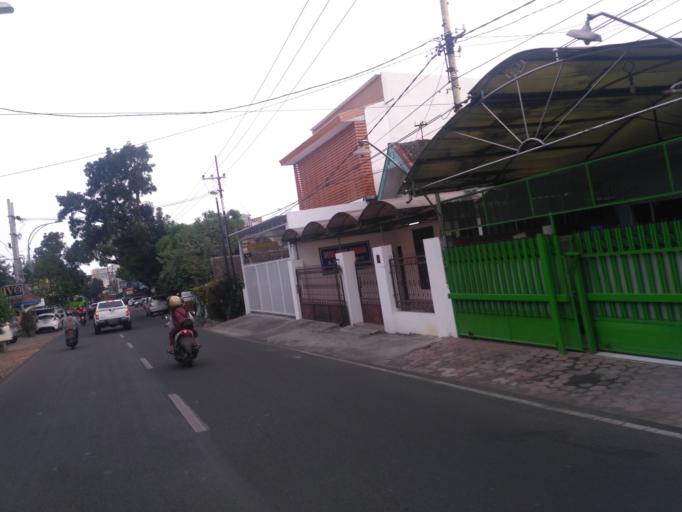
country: ID
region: East Java
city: Malang
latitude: -7.9704
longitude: 112.6287
